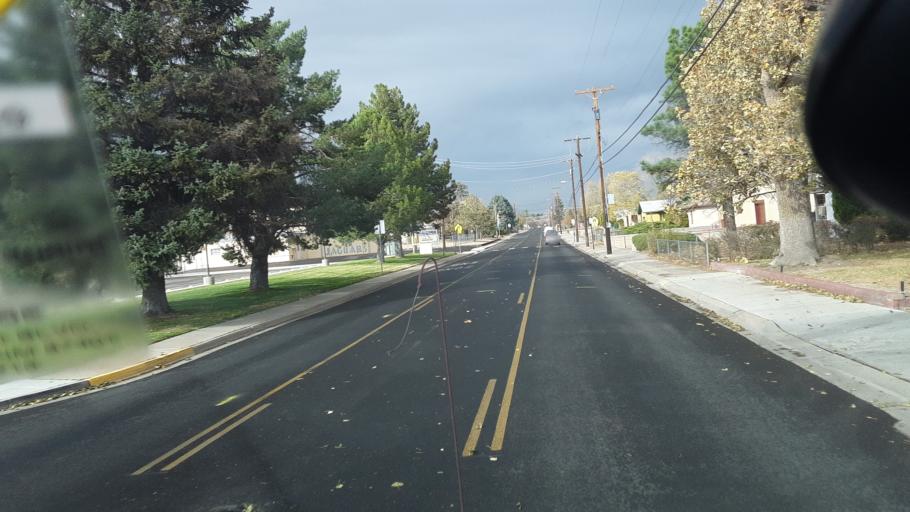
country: US
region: New Mexico
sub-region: San Juan County
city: Farmington
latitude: 36.7430
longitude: -108.1978
